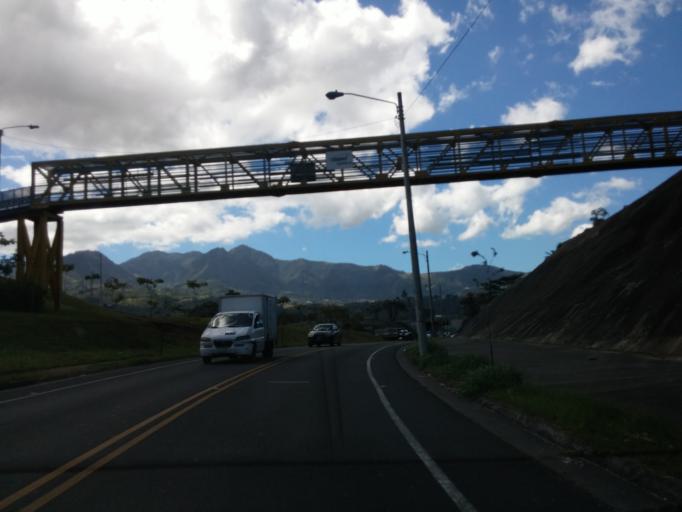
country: CR
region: San Jose
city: San Felipe
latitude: 9.9240
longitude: -84.1056
